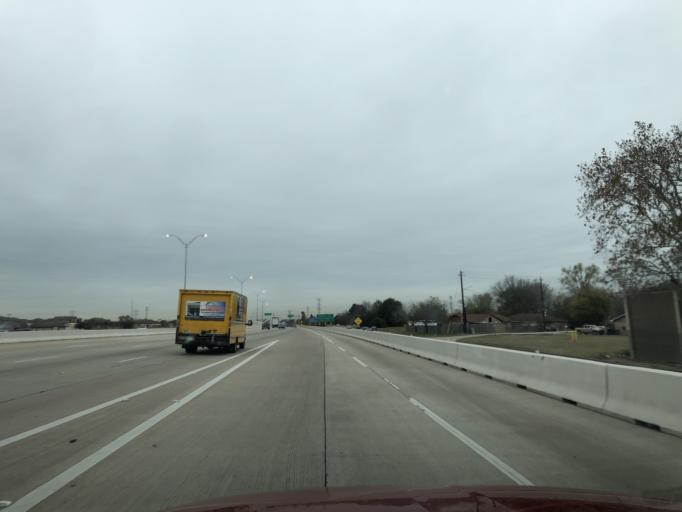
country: US
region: Texas
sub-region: Fort Bend County
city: Missouri City
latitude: 29.6171
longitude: -95.5003
